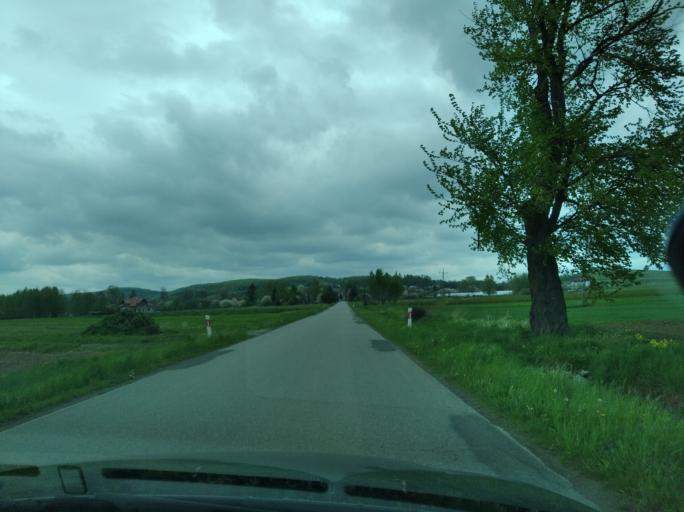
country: PL
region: Subcarpathian Voivodeship
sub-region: Powiat sanocki
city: Dlugie
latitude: 49.5988
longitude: 22.0511
